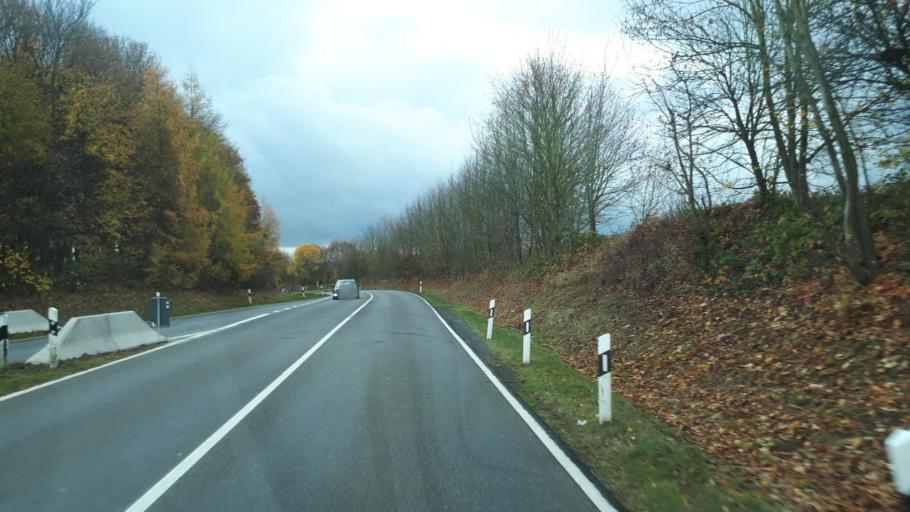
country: DE
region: Rheinland-Pfalz
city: Monreal
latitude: 50.3148
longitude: 7.1877
